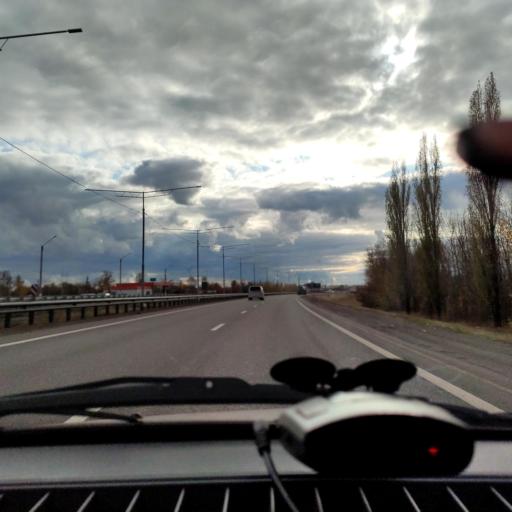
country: RU
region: Voronezj
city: Ramon'
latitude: 51.9938
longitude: 39.2192
